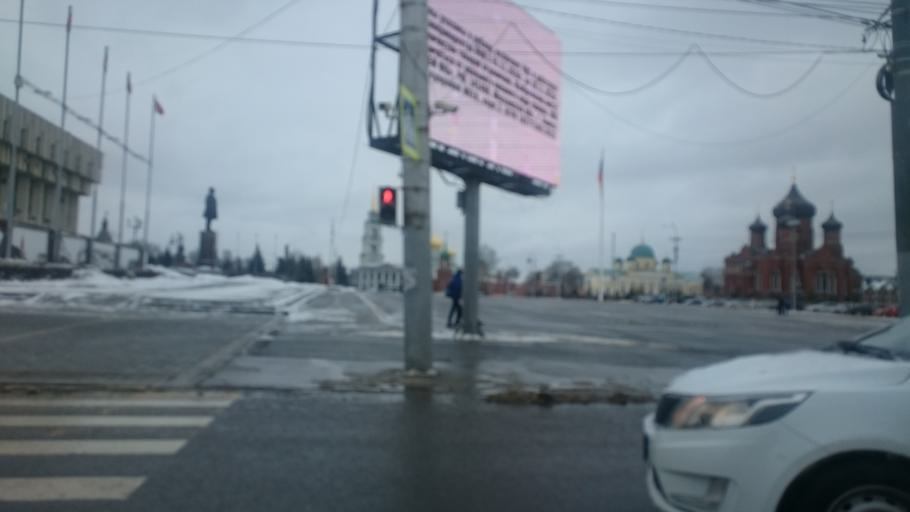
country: RU
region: Tula
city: Tula
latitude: 54.1922
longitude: 37.6164
